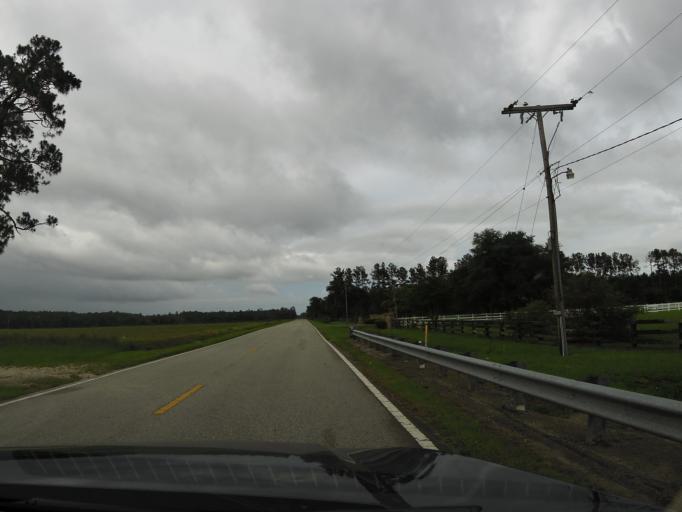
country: US
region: Florida
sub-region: Saint Johns County
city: Saint Augustine South
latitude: 29.8519
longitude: -81.4857
